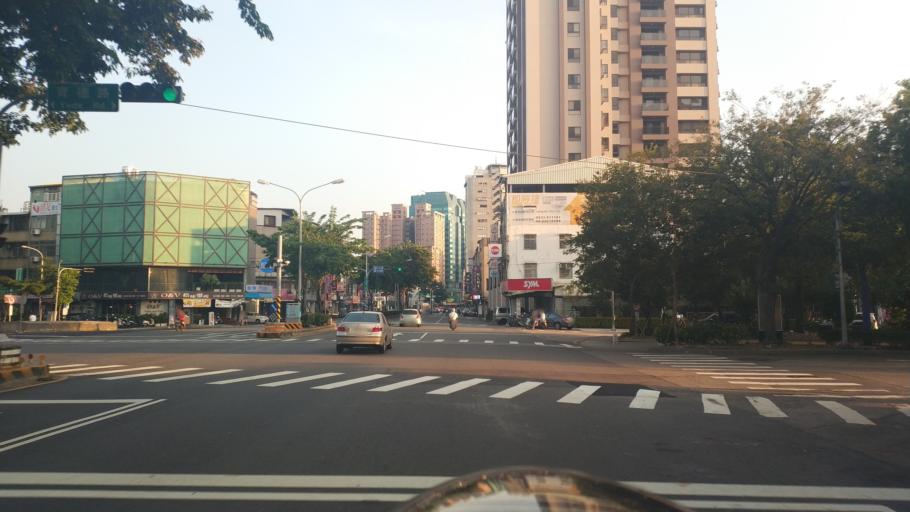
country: TW
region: Taiwan
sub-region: Taichung City
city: Taichung
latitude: 24.1578
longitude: 120.6761
